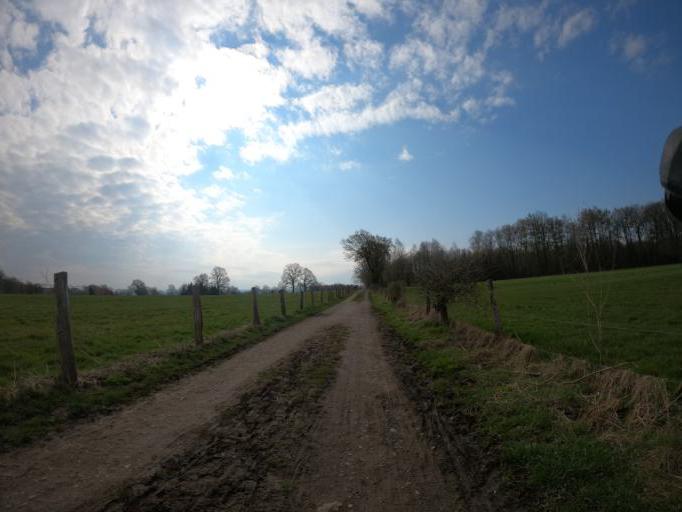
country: BE
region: Wallonia
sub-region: Province de Liege
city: Raeren
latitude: 50.7113
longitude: 6.1332
